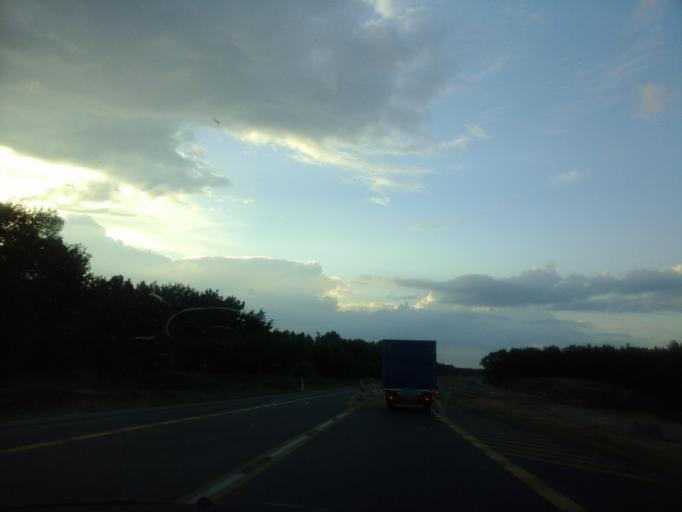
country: PL
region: Lubusz
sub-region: Powiat nowosolski
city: Nowa Sol
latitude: 51.7766
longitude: 15.6744
